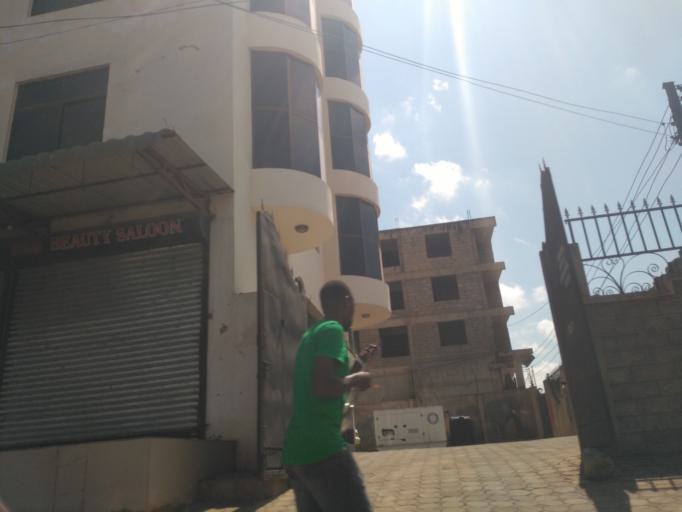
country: TZ
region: Arusha
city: Arusha
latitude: -3.3696
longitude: 36.6812
